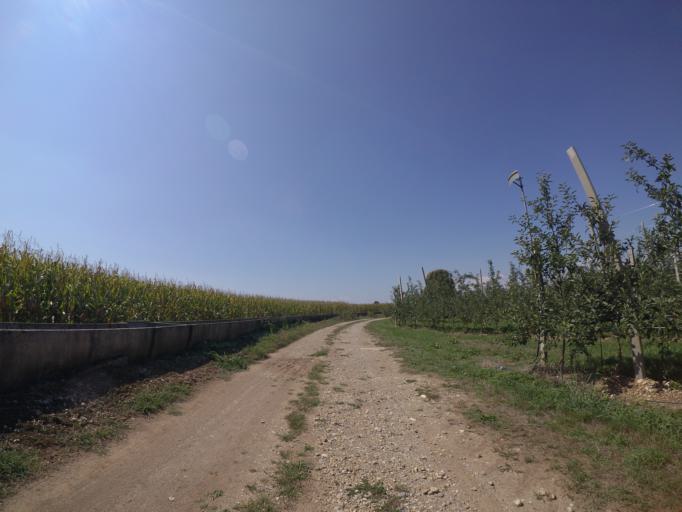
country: IT
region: Friuli Venezia Giulia
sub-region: Provincia di Udine
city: Bertiolo
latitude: 45.9428
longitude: 13.0672
